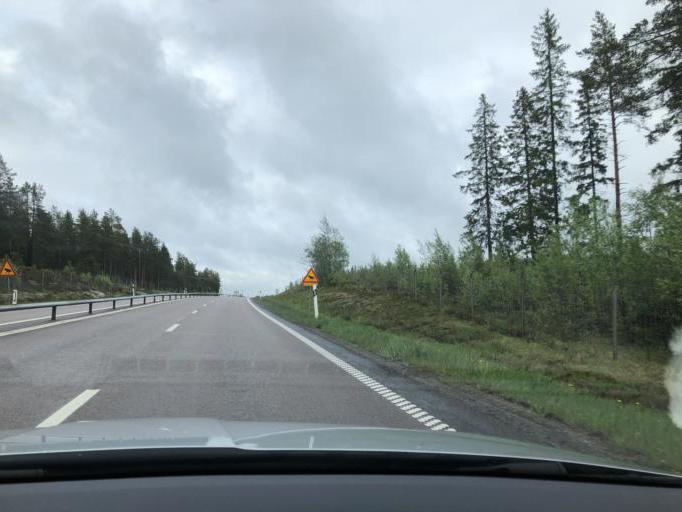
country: SE
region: Vaesternorrland
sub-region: OErnskoeldsviks Kommun
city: Husum
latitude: 63.3143
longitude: 18.9669
